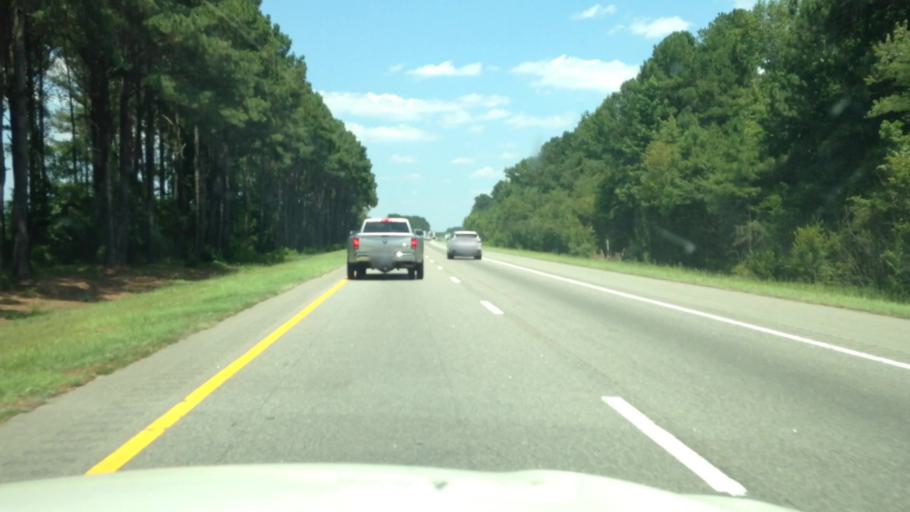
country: US
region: North Carolina
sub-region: Robeson County
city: Fairmont
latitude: 34.5833
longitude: -79.1372
